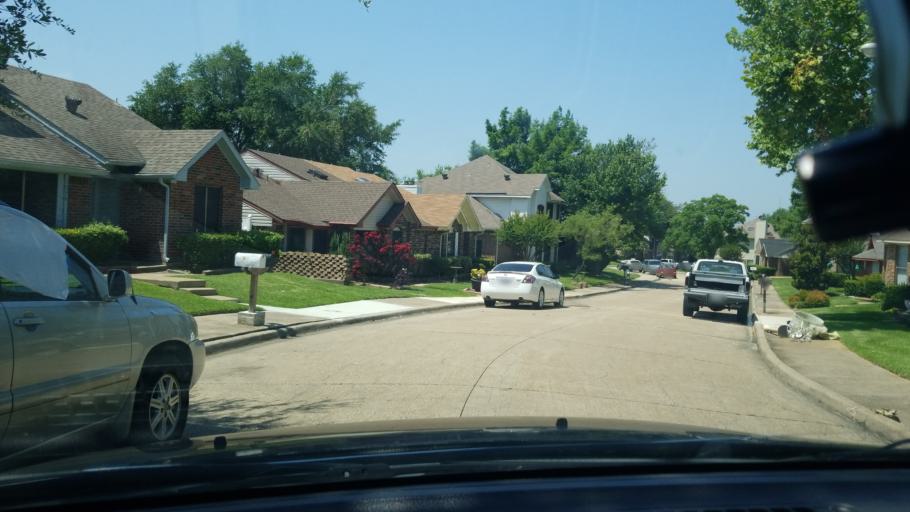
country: US
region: Texas
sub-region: Dallas County
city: Sunnyvale
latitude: 32.8305
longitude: -96.6127
